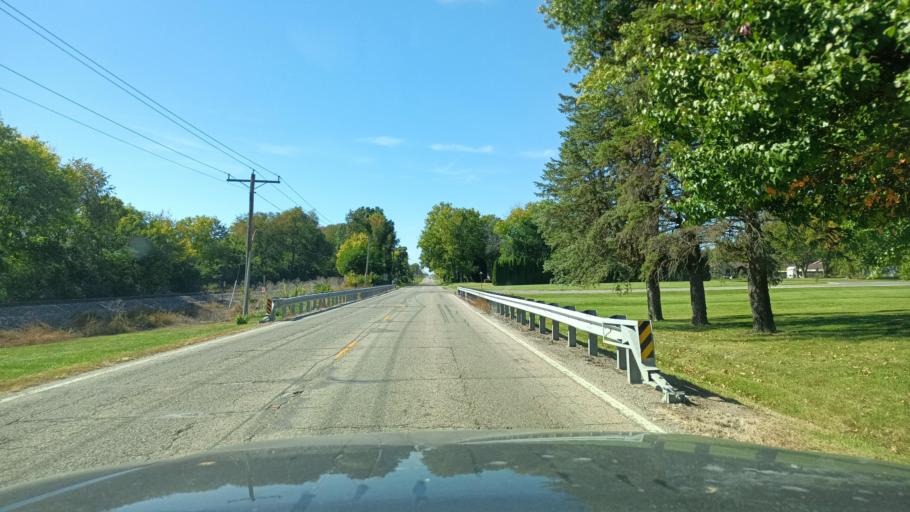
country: US
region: Illinois
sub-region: Champaign County
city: Mahomet
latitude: 40.1945
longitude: -88.4221
